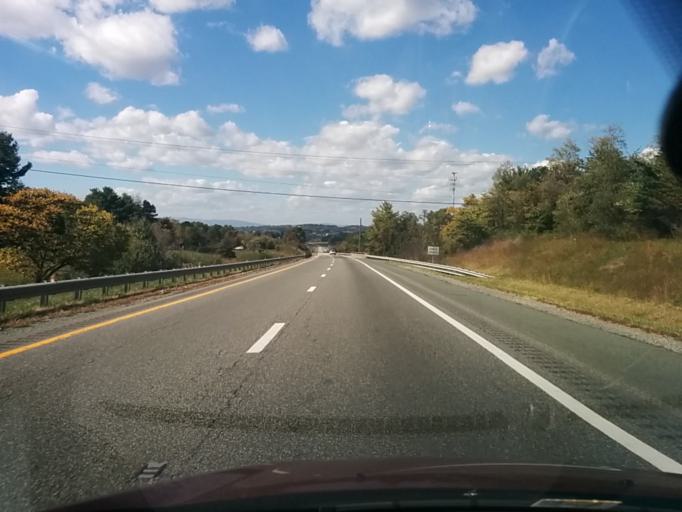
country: US
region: Virginia
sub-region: City of Waynesboro
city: Waynesboro
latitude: 38.0464
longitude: -78.9044
